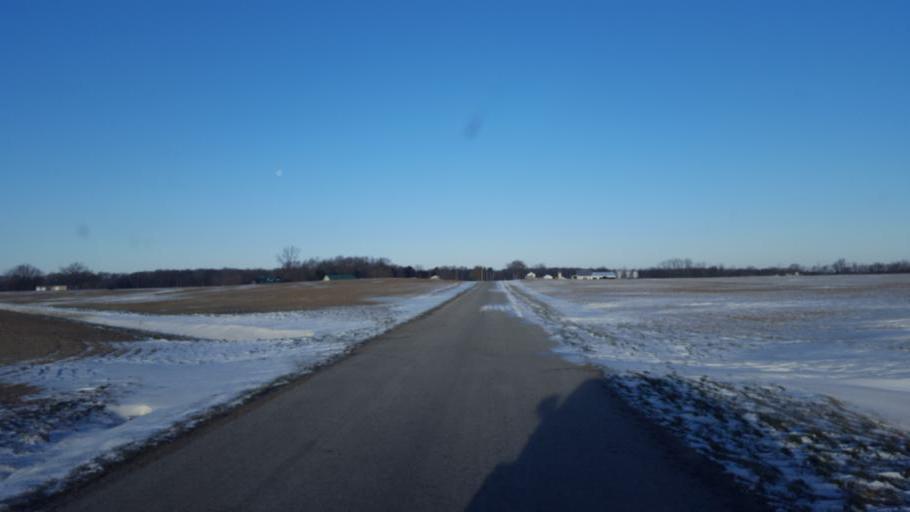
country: US
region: Ohio
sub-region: Morrow County
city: Cardington
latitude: 40.5164
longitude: -82.8910
